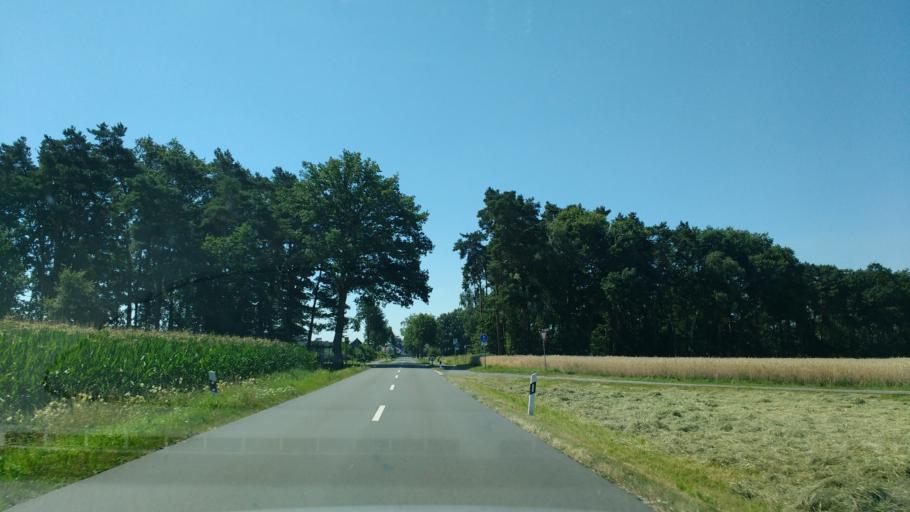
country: DE
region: North Rhine-Westphalia
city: Geseke
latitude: 51.7148
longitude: 8.4922
